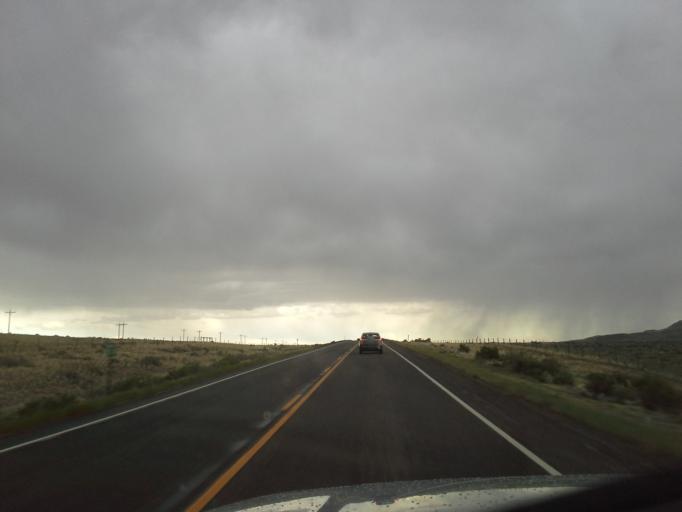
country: US
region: Wyoming
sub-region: Park County
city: Powell
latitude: 45.0401
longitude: -108.6465
